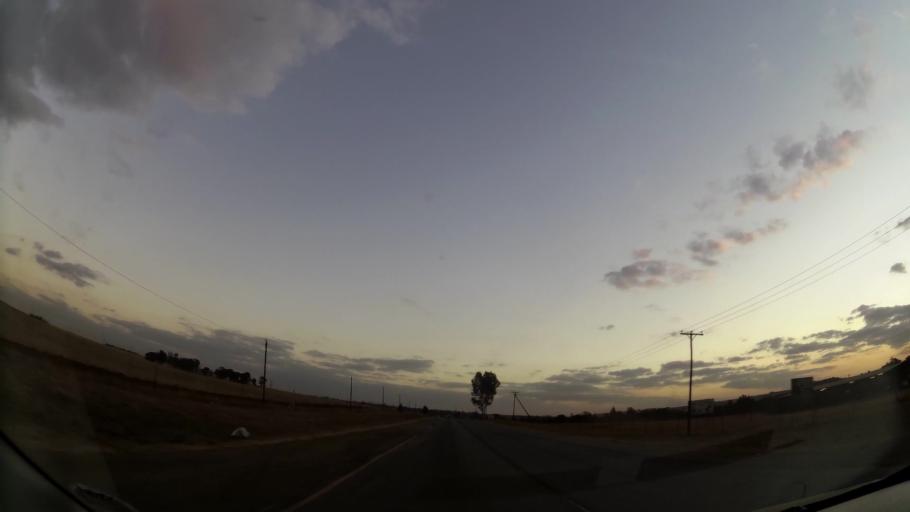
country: ZA
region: Gauteng
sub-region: West Rand District Municipality
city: Krugersdorp
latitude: -26.0551
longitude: 27.7070
